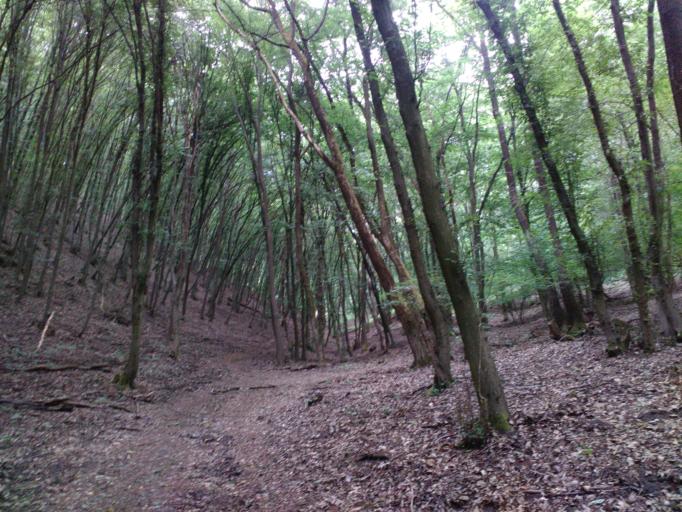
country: HU
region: Komarom-Esztergom
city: Esztergom
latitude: 47.8070
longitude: 18.8038
